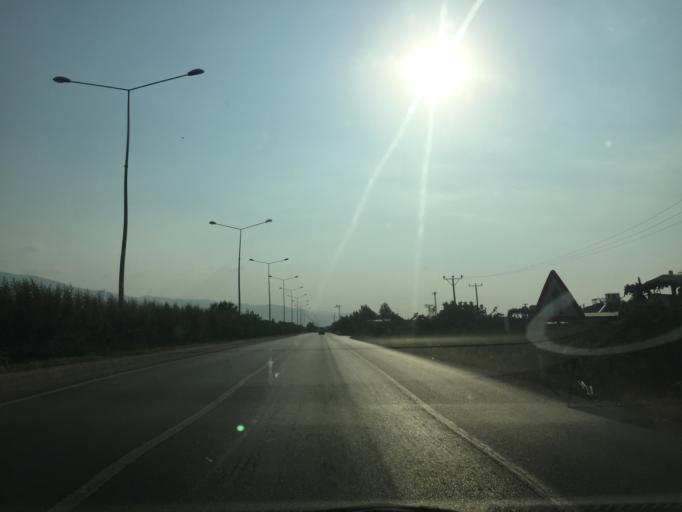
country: TR
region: Manisa
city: Salihli
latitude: 38.4928
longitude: 28.1714
